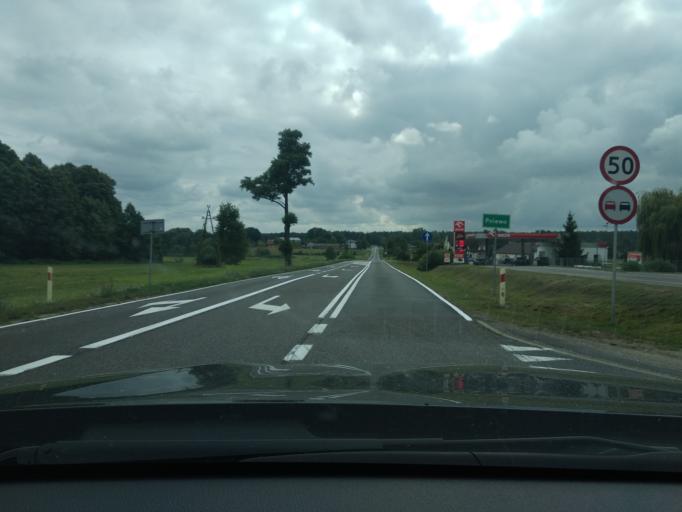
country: PL
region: Masovian Voivodeship
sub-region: Powiat pultuski
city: Obryte
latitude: 52.6503
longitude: 21.2437
